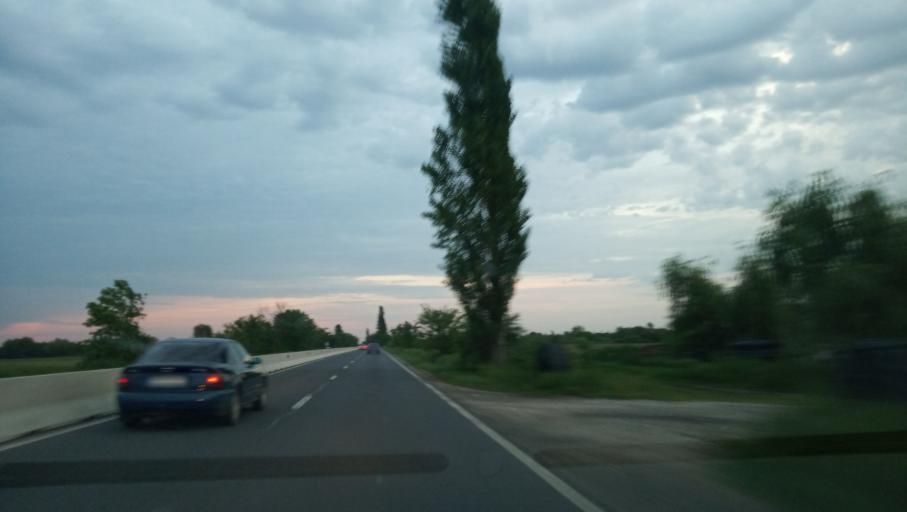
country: RO
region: Timis
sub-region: Comuna Sag
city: Sag
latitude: 45.6626
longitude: 21.1729
